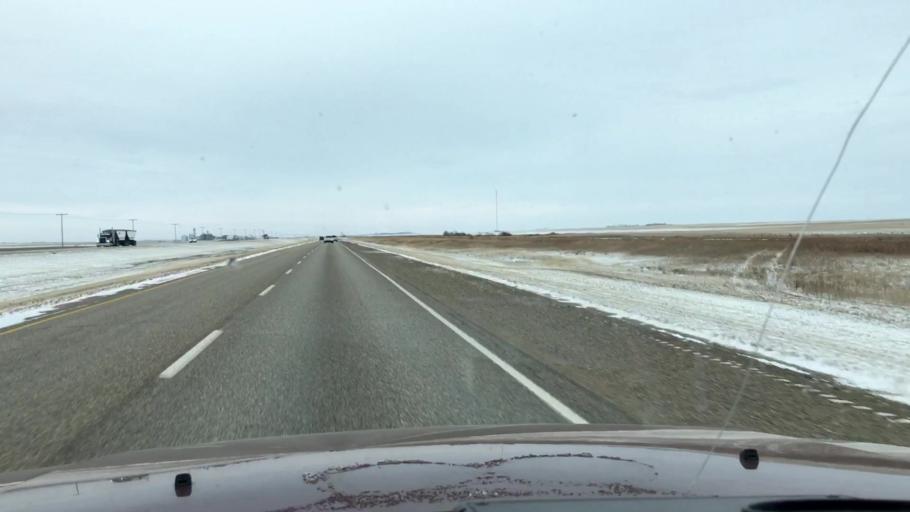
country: CA
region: Saskatchewan
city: Moose Jaw
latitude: 51.0230
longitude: -105.7894
